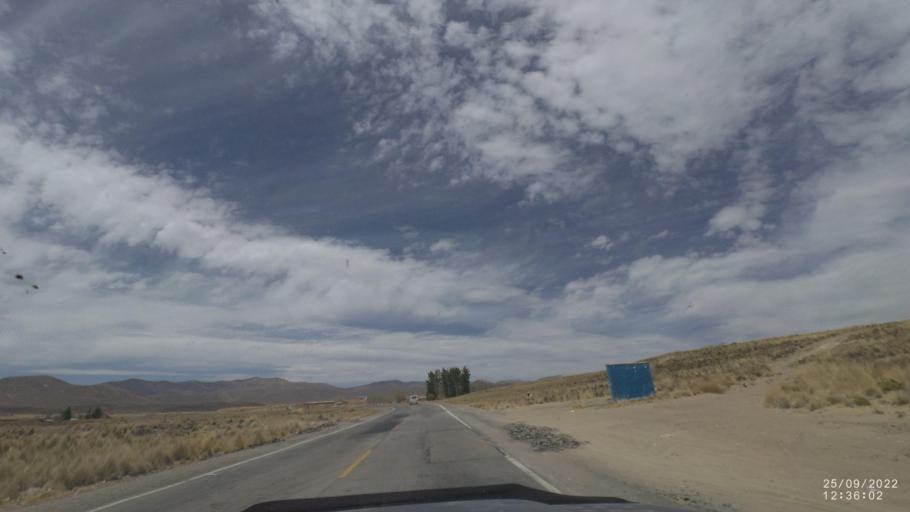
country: BO
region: Oruro
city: Machacamarca
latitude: -18.1665
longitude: -66.9933
